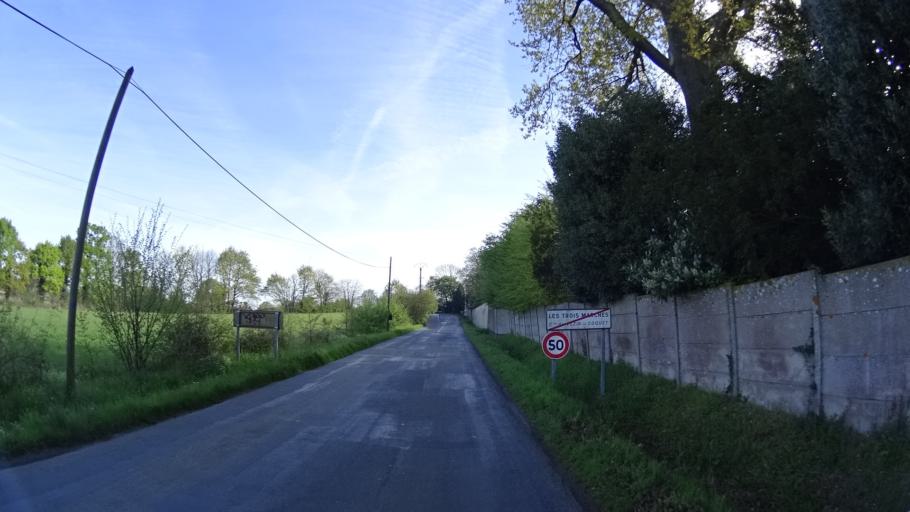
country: FR
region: Brittany
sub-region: Departement d'Ille-et-Vilaine
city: Vezin-le-Coquet
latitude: 48.1081
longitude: -1.7439
